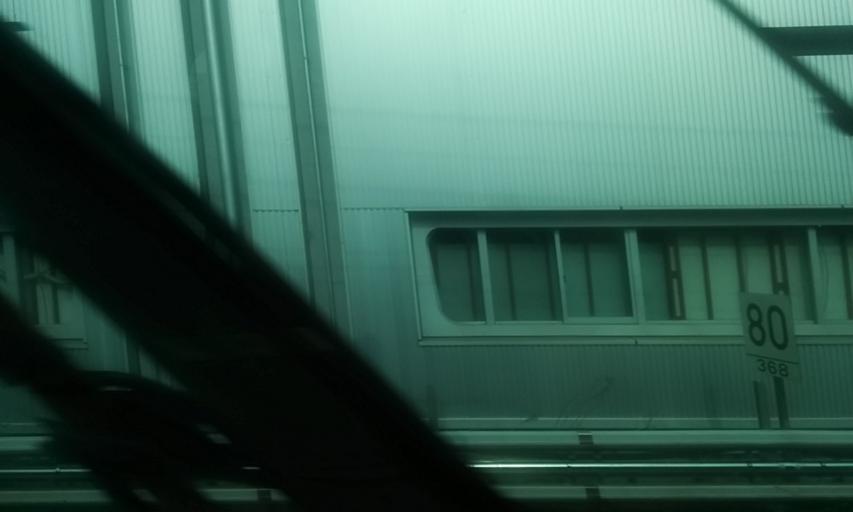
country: JP
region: Kanagawa
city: Yokohama
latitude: 35.4644
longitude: 139.6212
